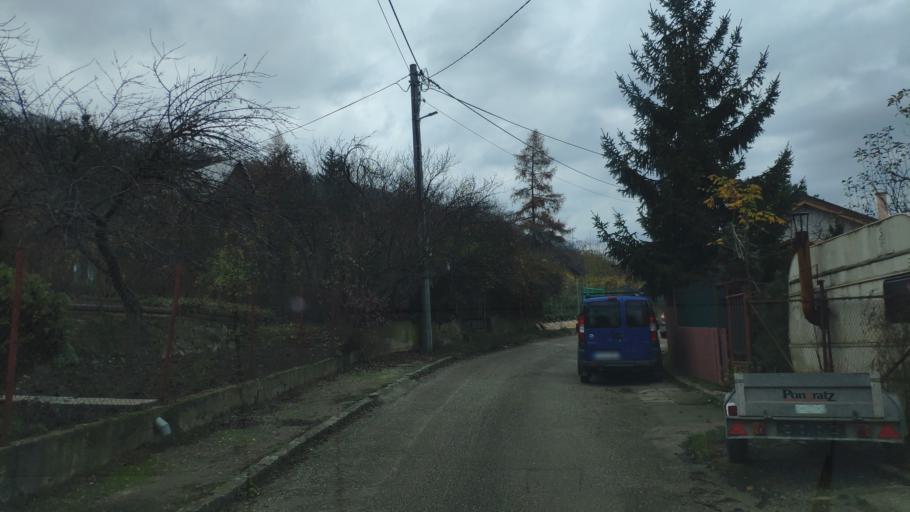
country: SK
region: Kosicky
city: Kosice
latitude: 48.6992
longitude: 21.2876
